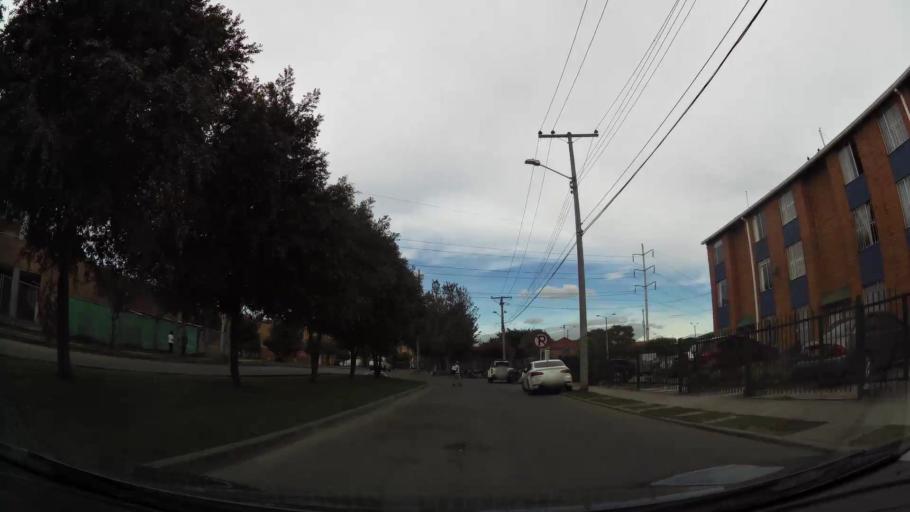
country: CO
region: Cundinamarca
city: Mosquera
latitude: 4.7072
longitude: -74.2220
